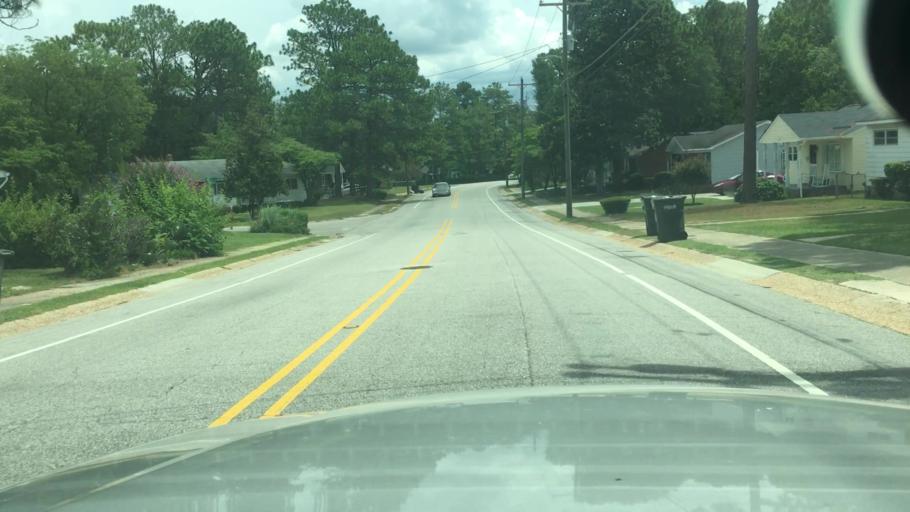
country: US
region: North Carolina
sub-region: Cumberland County
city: Fayetteville
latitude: 35.0815
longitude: -78.8956
